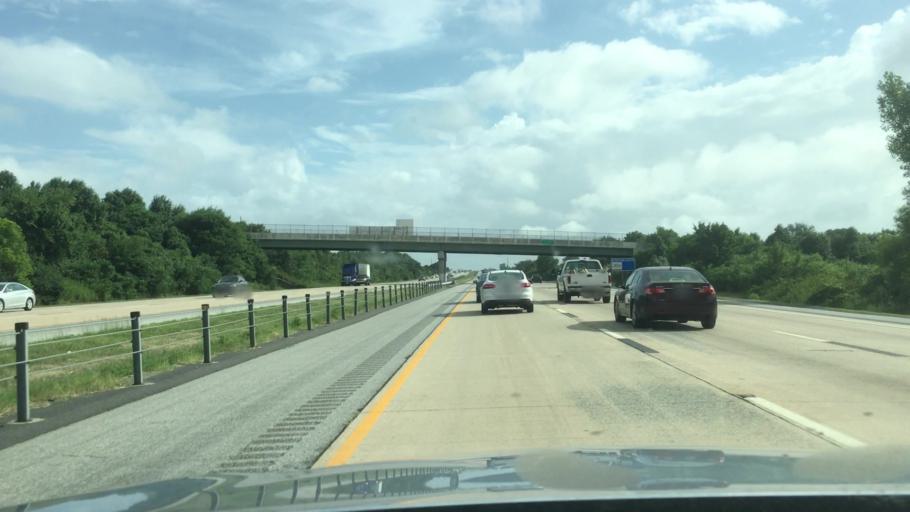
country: US
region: Delaware
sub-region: New Castle County
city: Bear
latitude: 39.5992
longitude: -75.6567
